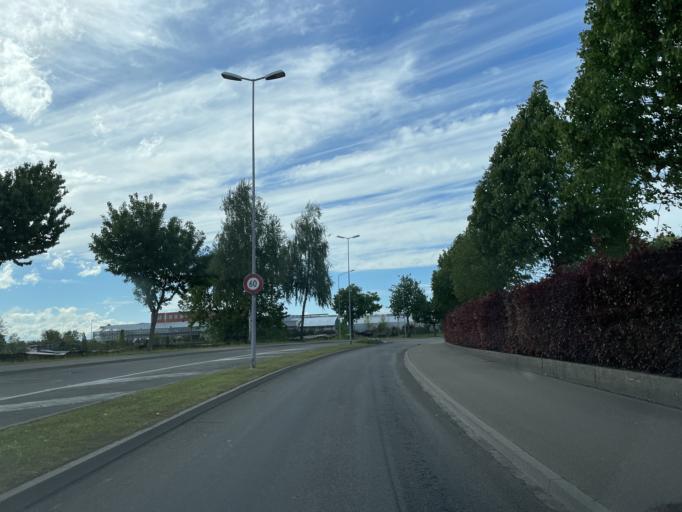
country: CH
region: Zurich
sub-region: Bezirk Uster
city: Wangen
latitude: 47.4130
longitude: 8.6385
